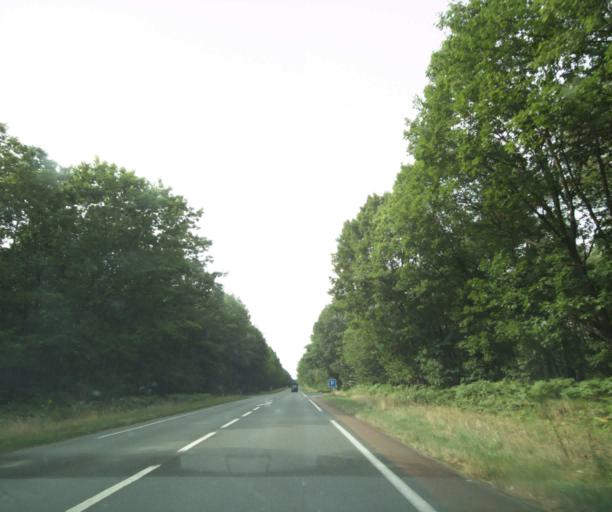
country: FR
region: Pays de la Loire
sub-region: Departement de la Sarthe
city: Marigne-Laille
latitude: 47.7660
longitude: 0.3524
